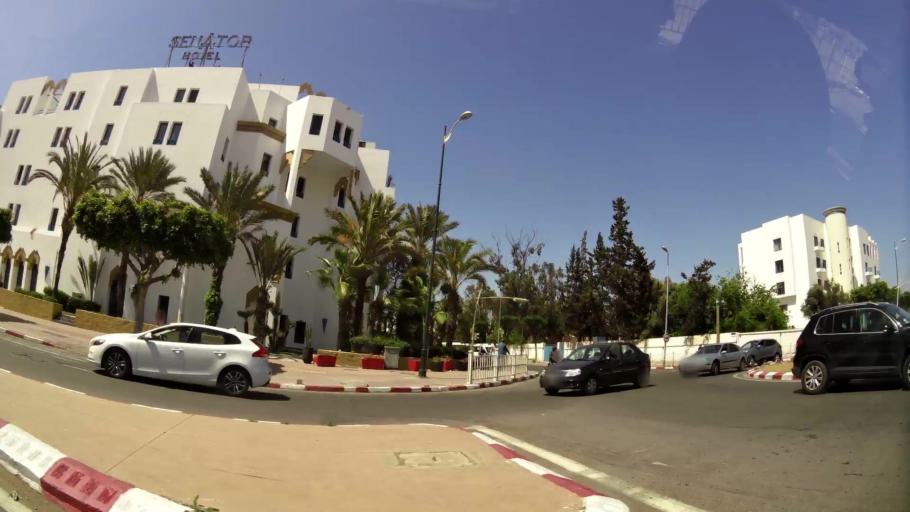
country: MA
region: Souss-Massa-Draa
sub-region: Agadir-Ida-ou-Tnan
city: Agadir
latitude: 30.4102
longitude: -9.5828
